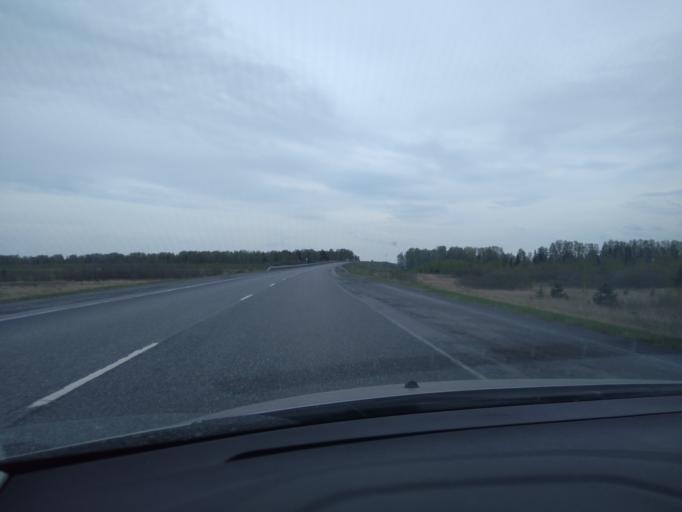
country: RU
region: Sverdlovsk
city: Kamyshlov
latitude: 56.8593
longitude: 62.8004
